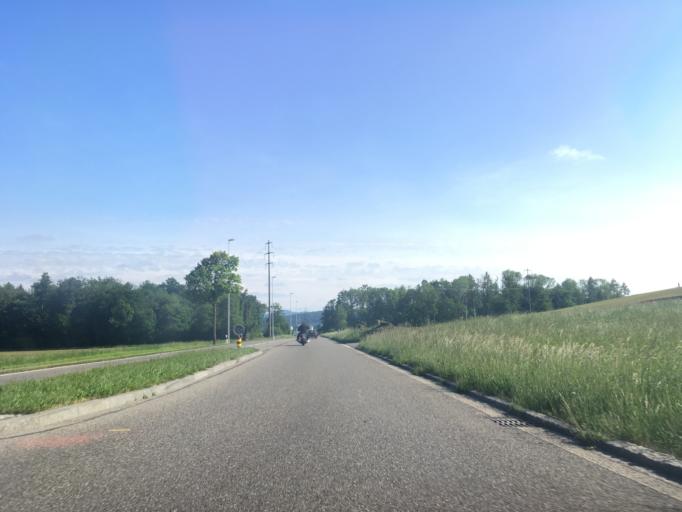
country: CH
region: Zurich
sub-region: Bezirk Dielsdorf
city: Sonnhalde
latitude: 47.4615
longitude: 8.4634
